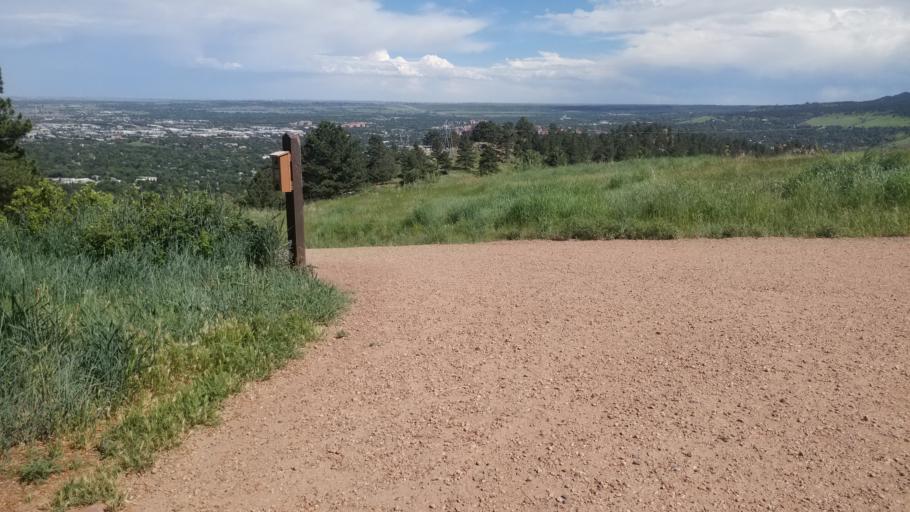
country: US
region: Colorado
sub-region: Boulder County
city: Boulder
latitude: 40.0359
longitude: -105.2990
